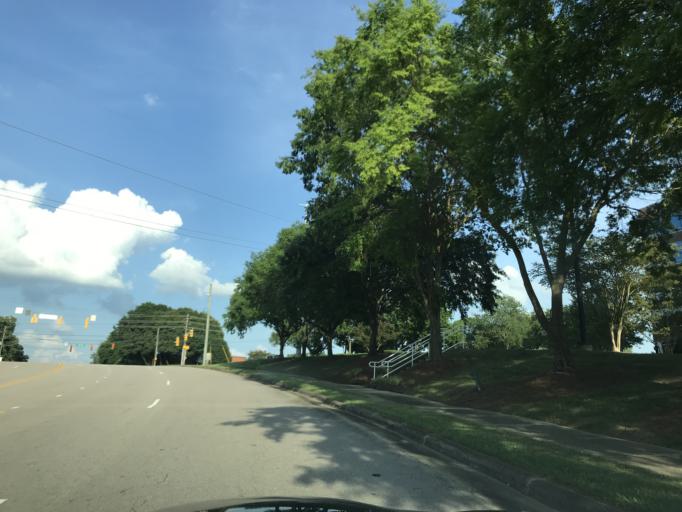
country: US
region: North Carolina
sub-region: Wake County
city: West Raleigh
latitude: 35.8155
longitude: -78.7064
